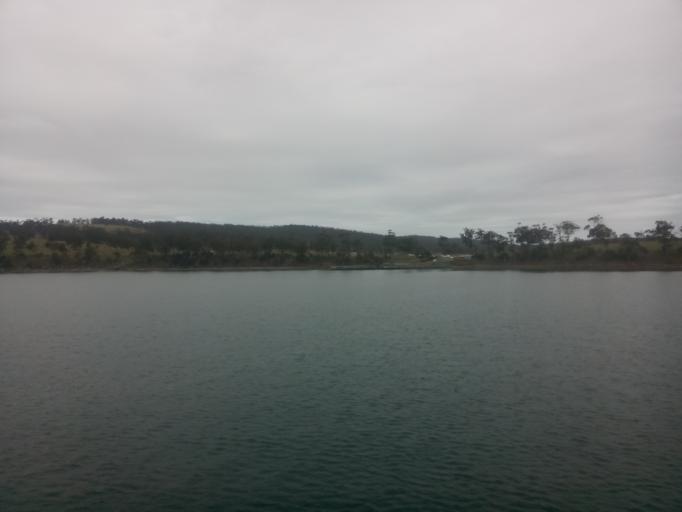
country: AU
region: Tasmania
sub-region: Kingborough
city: Kettering
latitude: -43.1400
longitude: 147.2832
